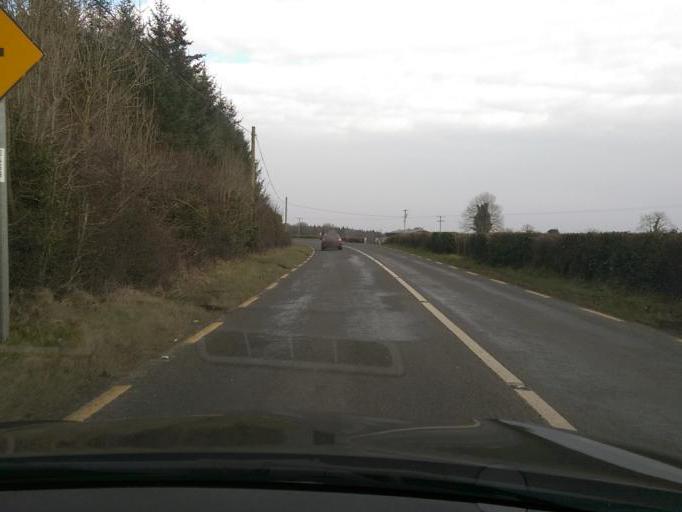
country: IE
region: Connaught
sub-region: Roscommon
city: Castlerea
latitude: 53.4959
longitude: -8.4703
